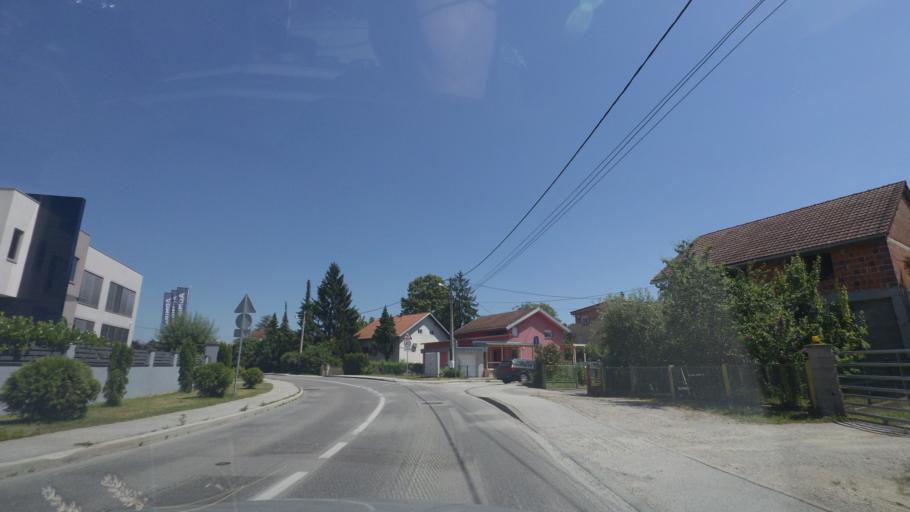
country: HR
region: Grad Zagreb
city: Zadvorsko
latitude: 45.7649
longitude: 15.9222
